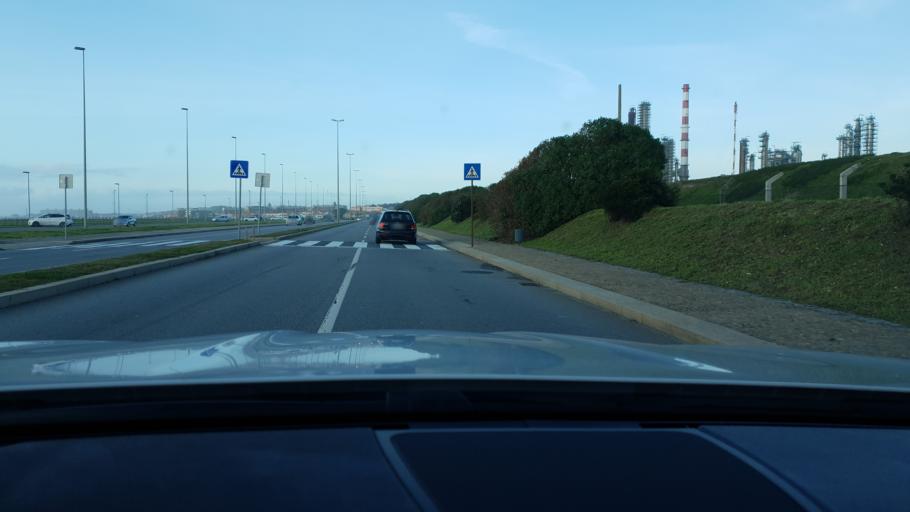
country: PT
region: Porto
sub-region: Matosinhos
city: Leca da Palmeira
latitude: 41.2144
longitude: -8.7130
